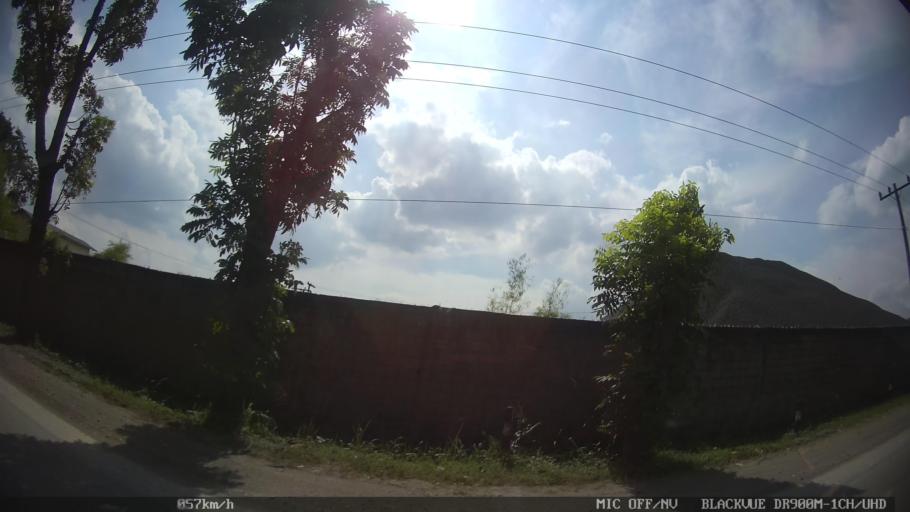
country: ID
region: North Sumatra
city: Binjai
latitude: 3.6212
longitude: 98.5346
